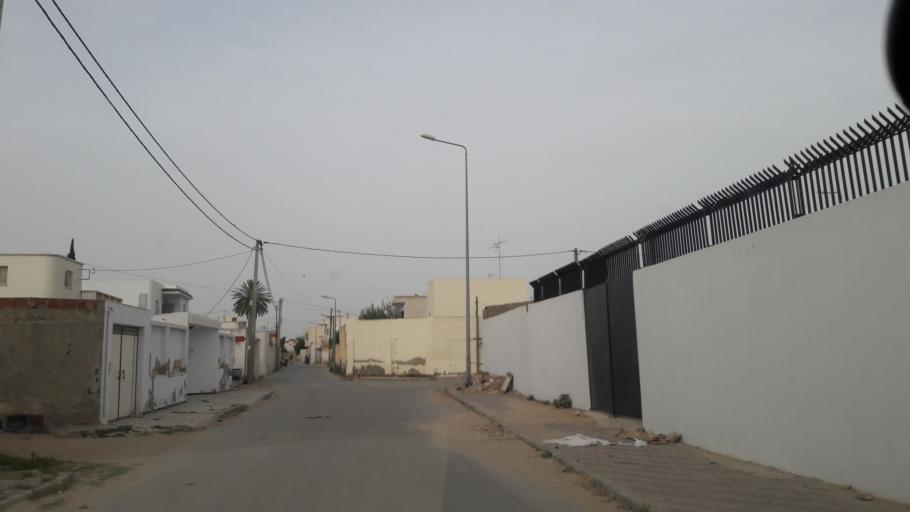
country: TN
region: Safaqis
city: Al Qarmadah
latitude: 34.7760
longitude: 10.7625
